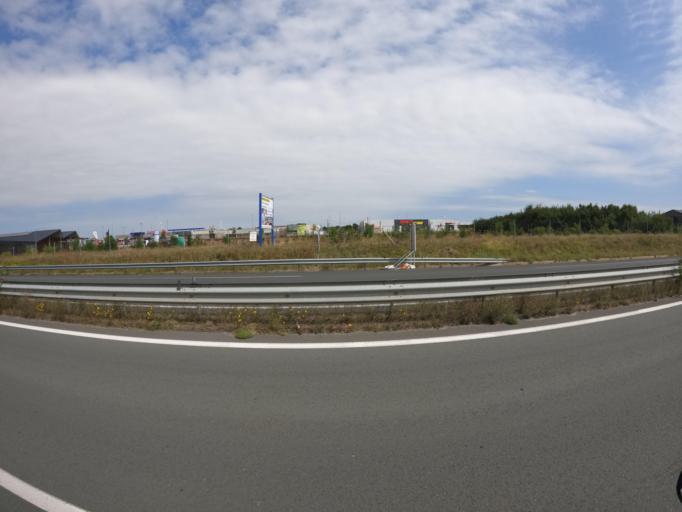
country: FR
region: Poitou-Charentes
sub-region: Departement de la Charente-Maritime
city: Saint-Jean-de-Liversay
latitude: 46.2261
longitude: -0.8721
